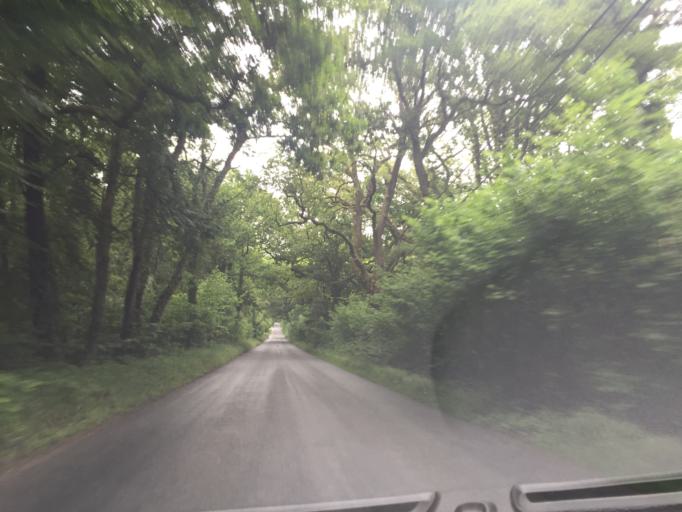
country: GB
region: England
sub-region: Dorset
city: Bovington Camp
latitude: 50.7195
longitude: -2.2774
